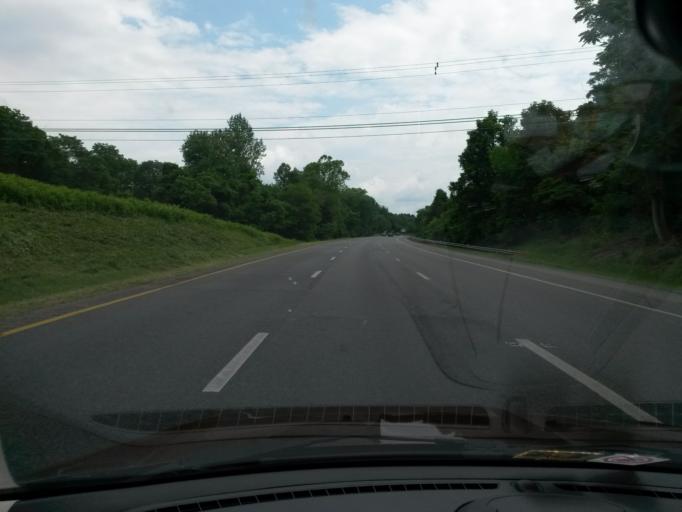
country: US
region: Virginia
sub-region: City of Charlottesville
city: Charlottesville
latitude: 38.0211
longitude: -78.4258
